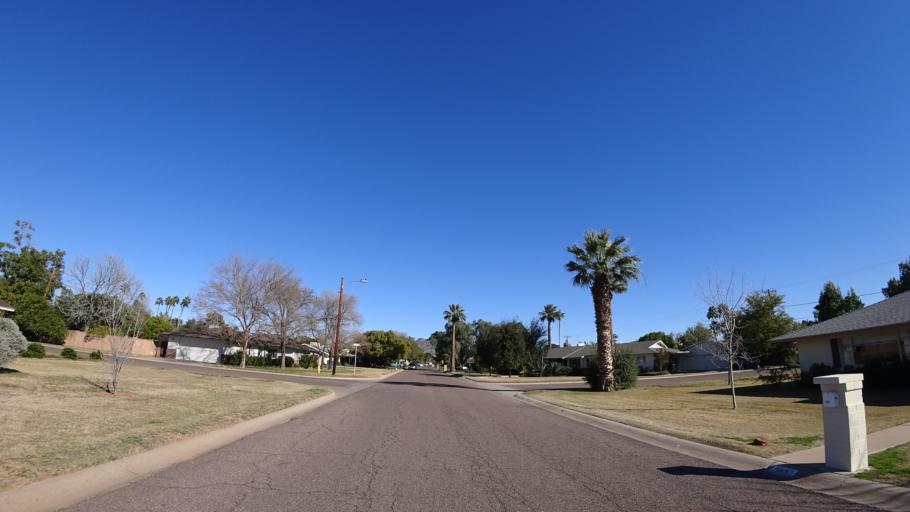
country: US
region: Arizona
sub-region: Maricopa County
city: Phoenix
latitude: 33.5496
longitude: -112.0719
